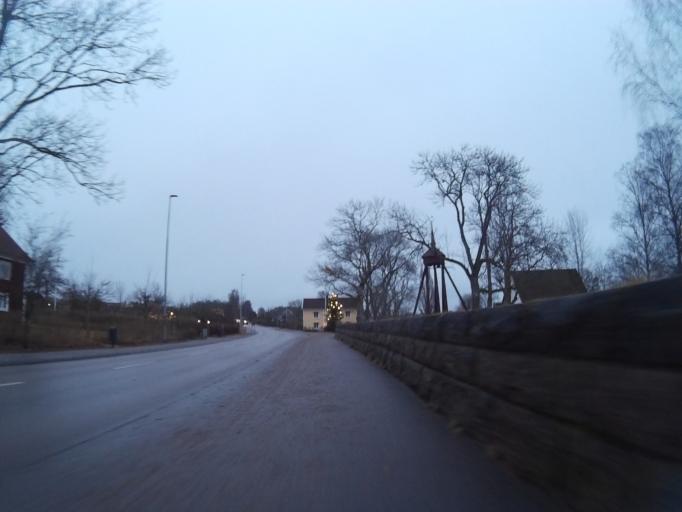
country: SE
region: Kronoberg
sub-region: Vaxjo Kommun
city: Vaexjoe
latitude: 56.9057
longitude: 14.7390
